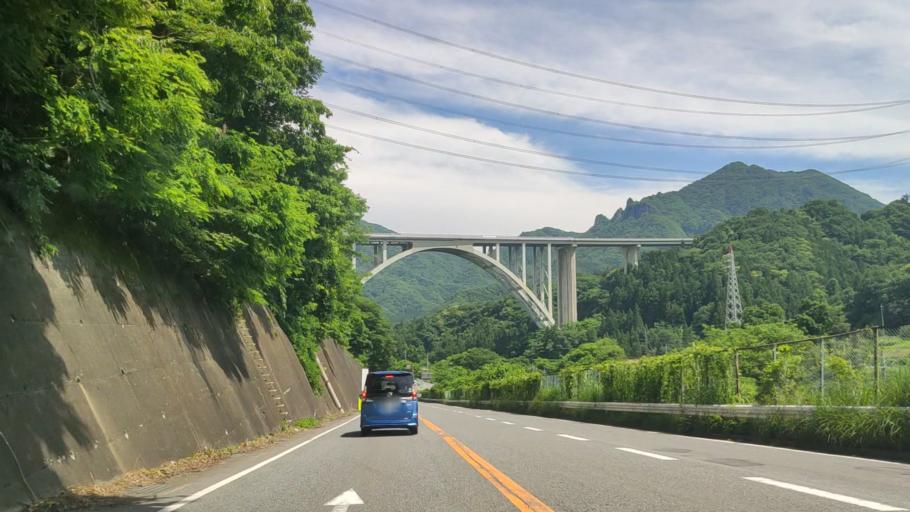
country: JP
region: Gunma
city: Annaka
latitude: 36.3285
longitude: 138.6877
